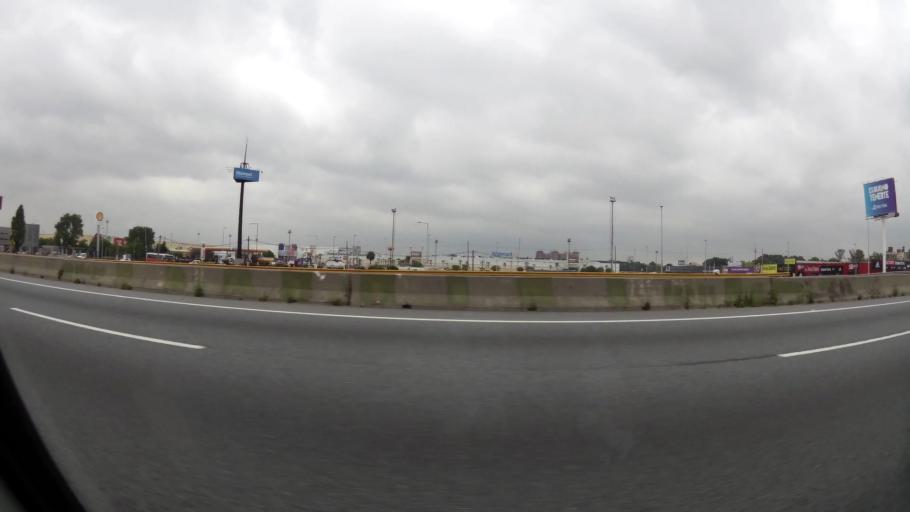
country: AR
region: Buenos Aires
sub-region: Partido de Avellaneda
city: Avellaneda
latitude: -34.6759
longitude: -58.3312
